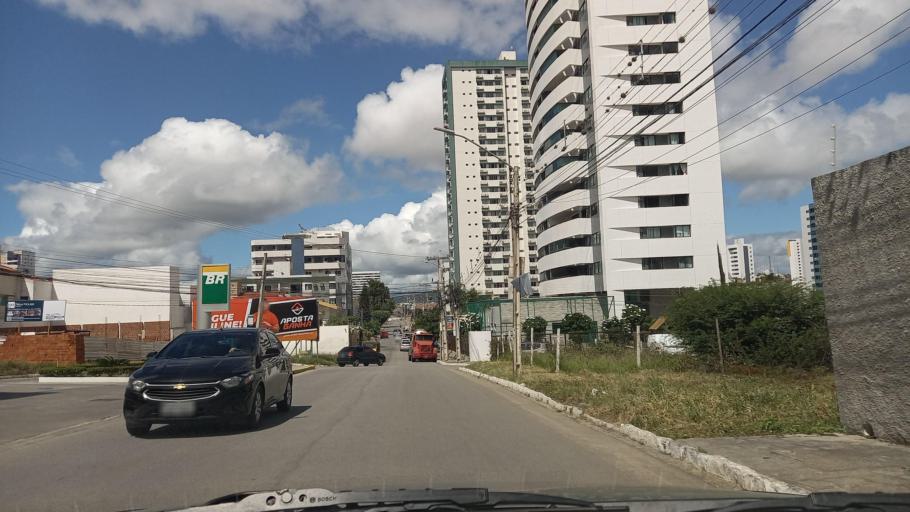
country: BR
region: Pernambuco
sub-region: Caruaru
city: Caruaru
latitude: -8.2648
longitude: -35.9663
